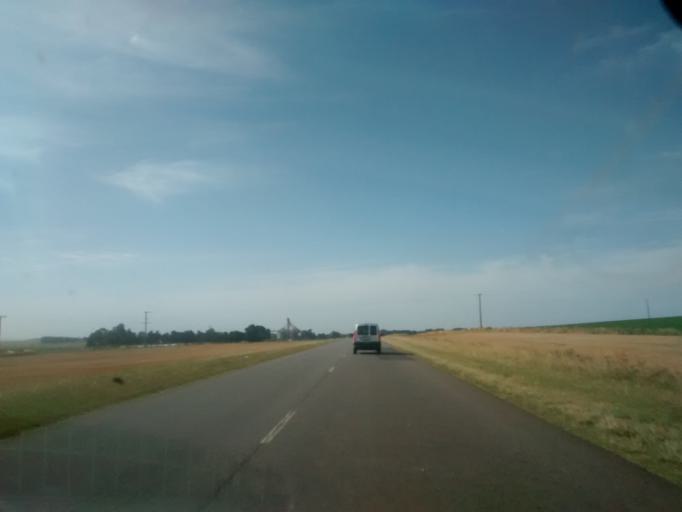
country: AR
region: Buenos Aires
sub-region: Partido de Loberia
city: Loberia
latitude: -37.6613
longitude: -58.7356
